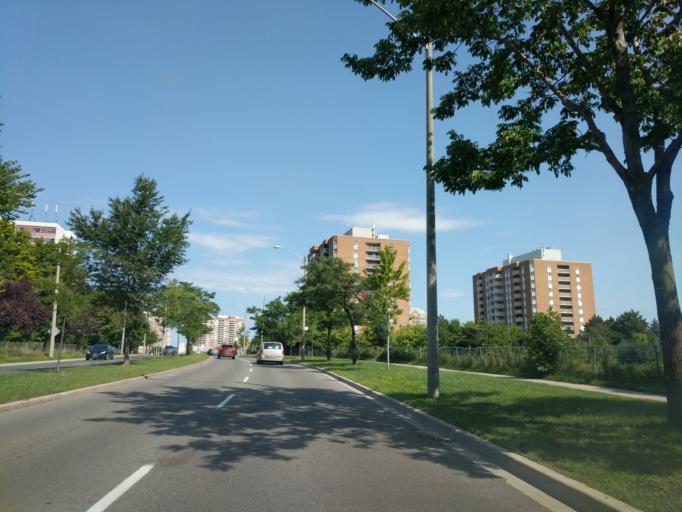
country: CA
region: Ontario
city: Scarborough
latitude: 43.8049
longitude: -79.2174
